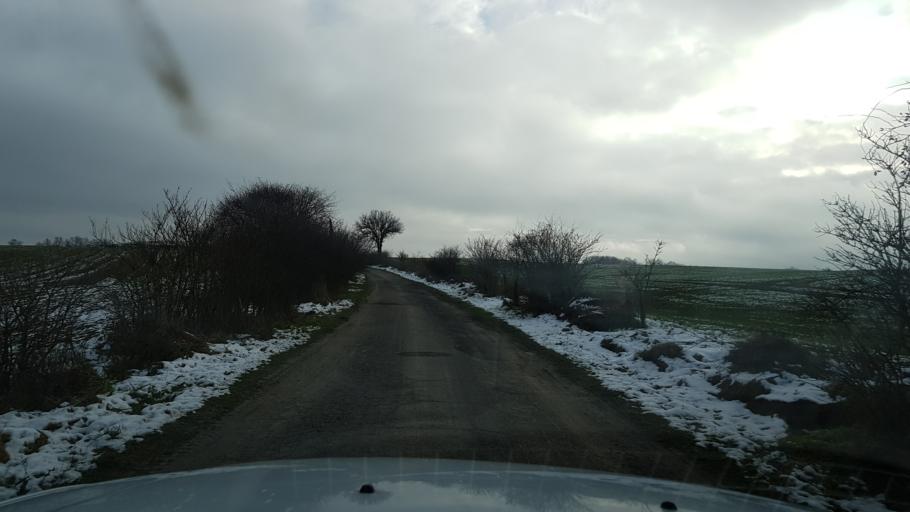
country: PL
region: West Pomeranian Voivodeship
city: Trzcinsko Zdroj
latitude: 52.9546
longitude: 14.6887
